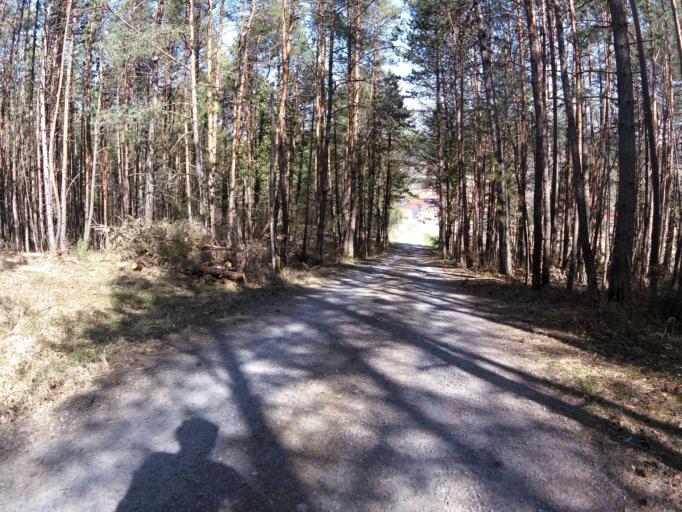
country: DE
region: Bavaria
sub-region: Regierungsbezirk Unterfranken
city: Erlabrunn
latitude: 49.8538
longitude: 9.8141
